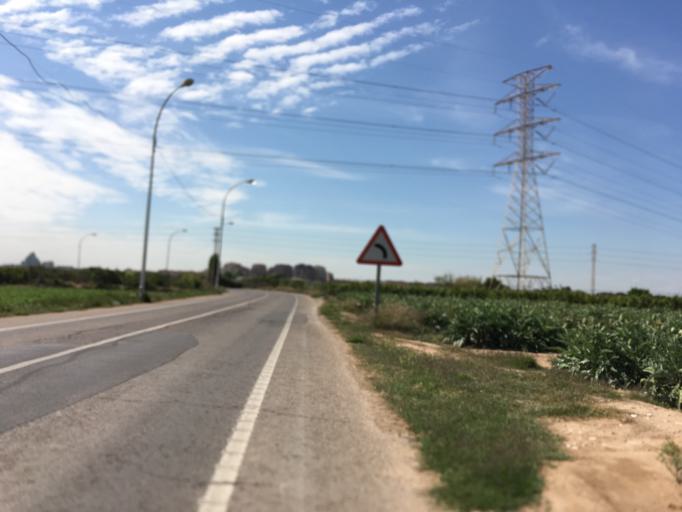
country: ES
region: Valencia
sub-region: Provincia de Valencia
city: Mislata
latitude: 39.4919
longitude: -0.4182
